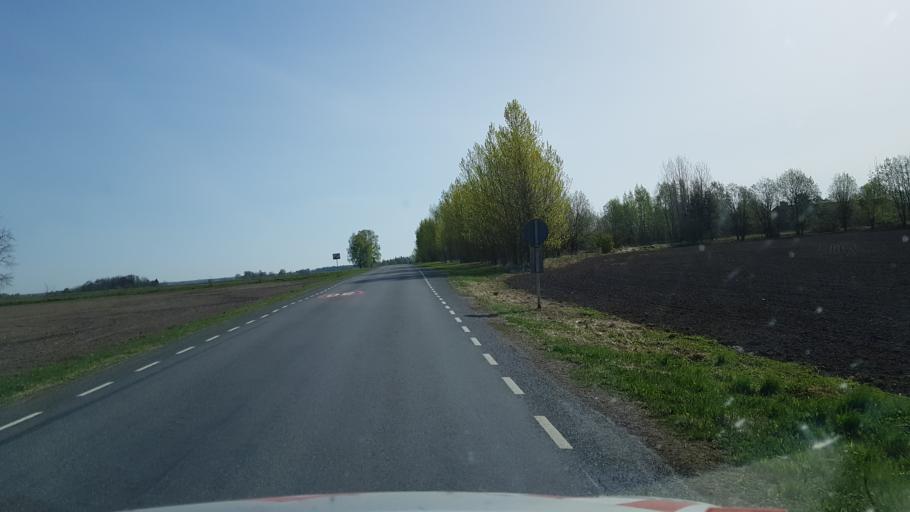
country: EE
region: Viljandimaa
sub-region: Abja vald
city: Abja-Paluoja
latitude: 58.1650
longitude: 25.4481
